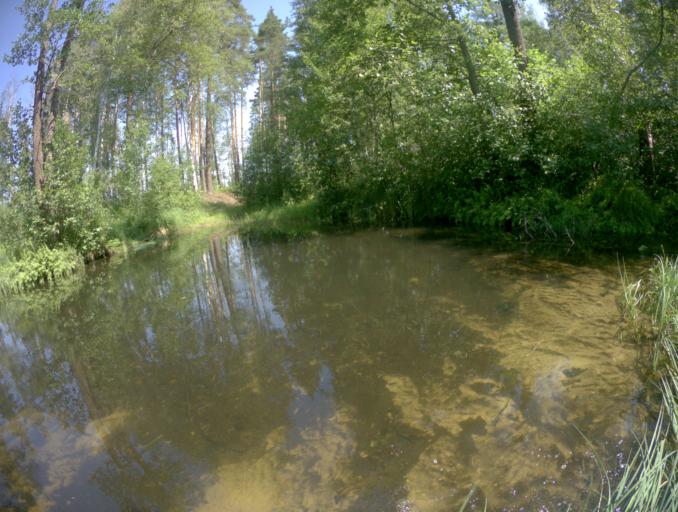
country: RU
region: Ivanovo
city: Talitsy
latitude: 56.4086
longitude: 42.2662
